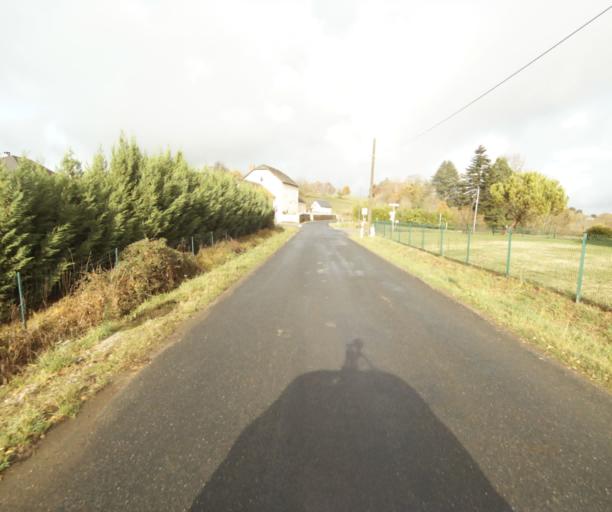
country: FR
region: Limousin
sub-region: Departement de la Correze
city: Cornil
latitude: 45.2126
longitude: 1.6421
